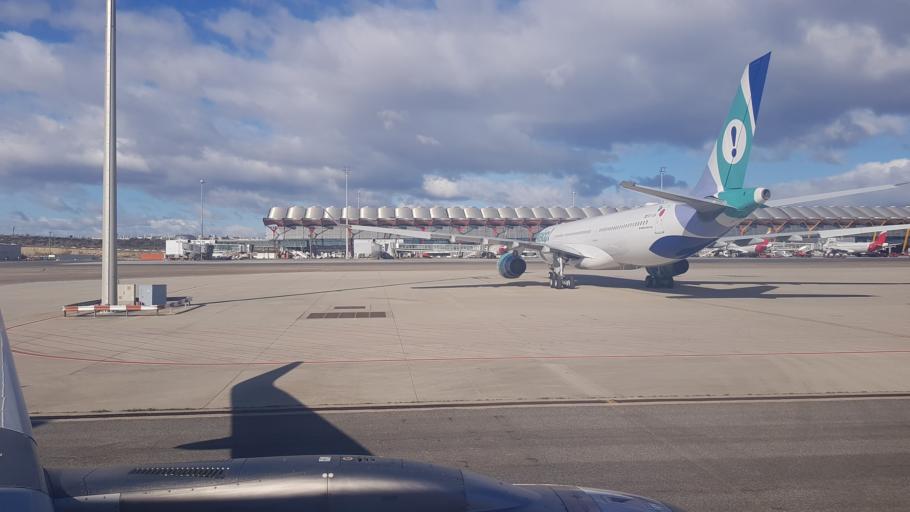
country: ES
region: Madrid
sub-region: Provincia de Madrid
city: Barajas de Madrid
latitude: 40.4865
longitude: -3.5865
